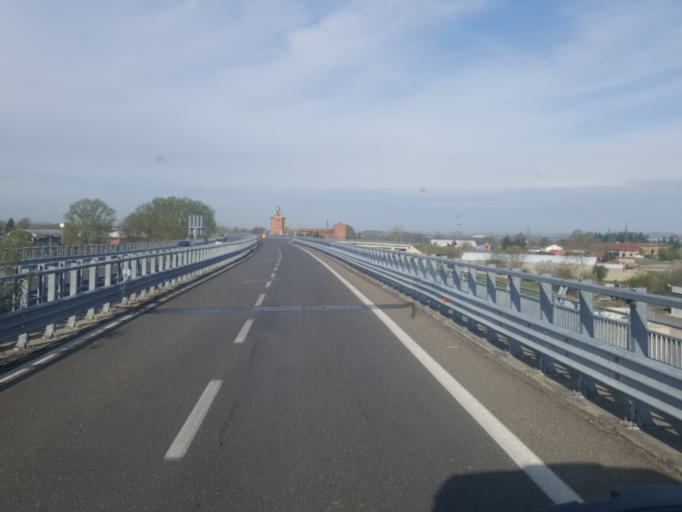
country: IT
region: Piedmont
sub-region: Provincia di Alessandria
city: Valle San Bartolomeo
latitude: 44.9351
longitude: 8.6190
